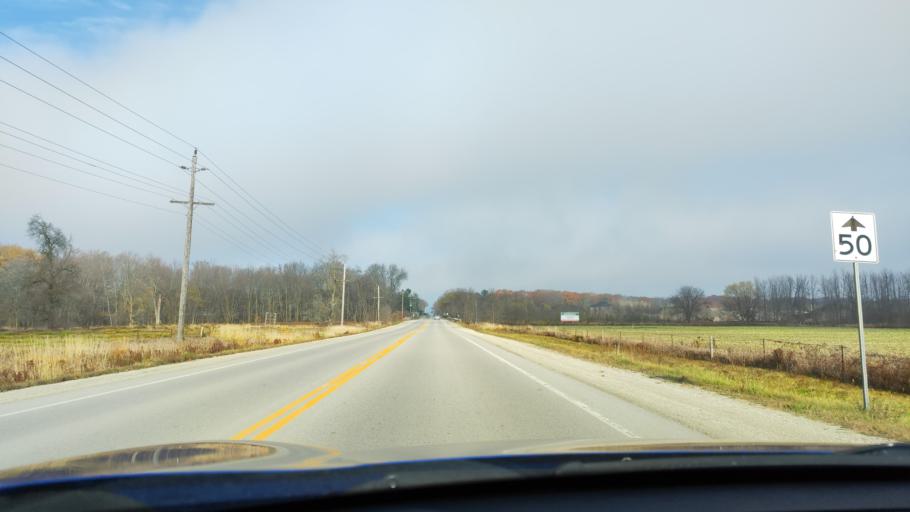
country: CA
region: Ontario
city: Wasaga Beach
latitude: 44.4596
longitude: -80.0725
